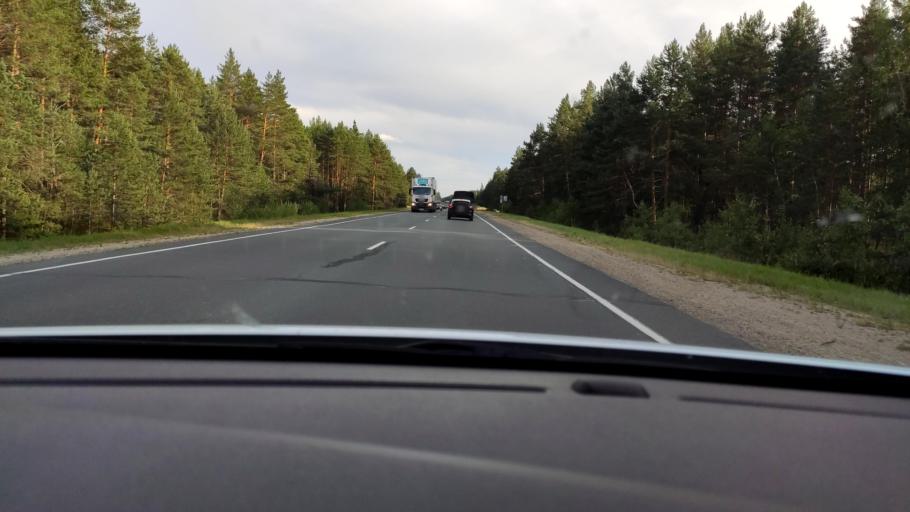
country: RU
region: Mariy-El
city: Krasnogorskiy
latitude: 56.0923
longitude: 48.3481
